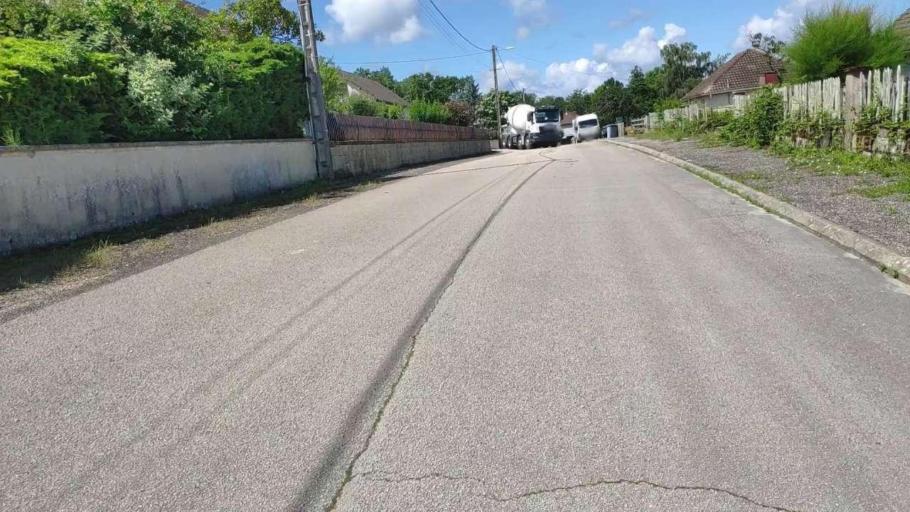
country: FR
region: Franche-Comte
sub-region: Departement du Jura
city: Bletterans
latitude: 46.8238
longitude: 5.5561
